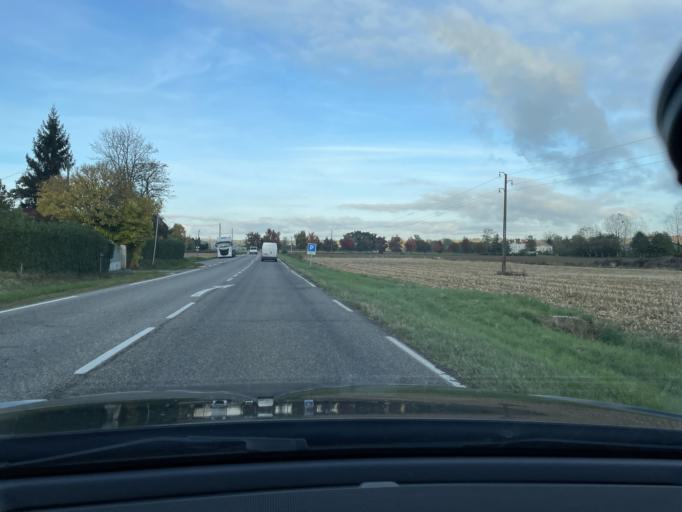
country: FR
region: Aquitaine
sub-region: Departement du Lot-et-Garonne
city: Fourques-sur-Garonne
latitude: 44.4018
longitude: 0.1221
